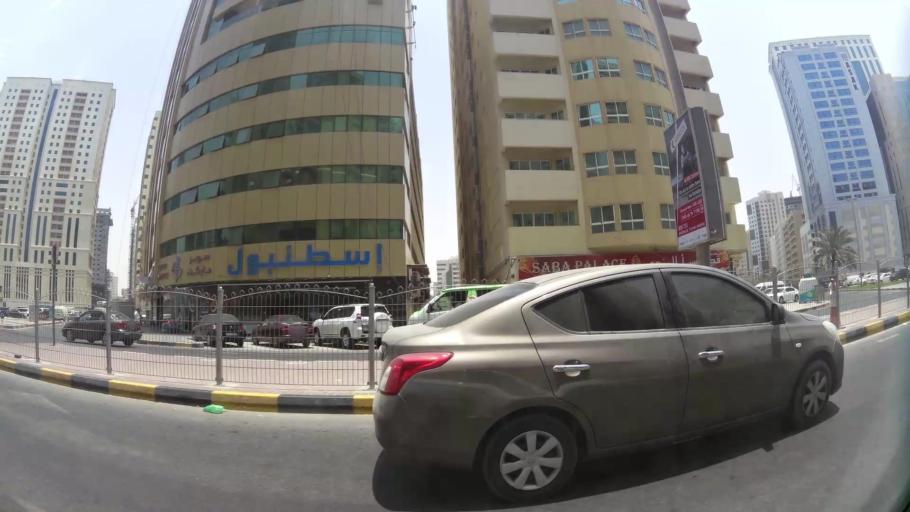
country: AE
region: Ash Shariqah
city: Sharjah
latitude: 25.3207
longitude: 55.3807
